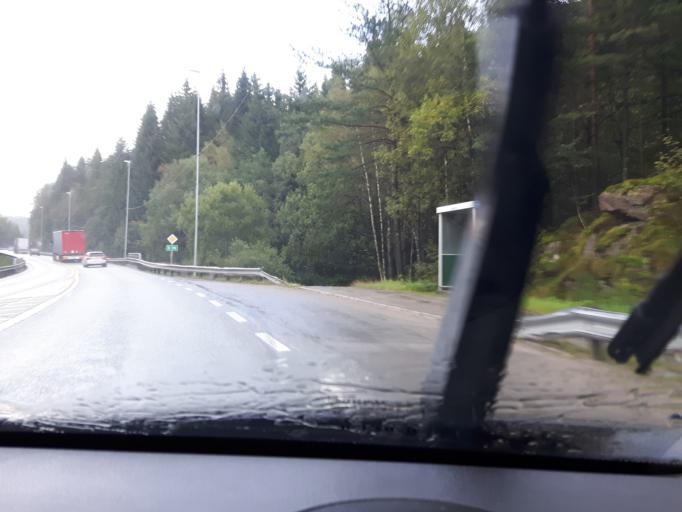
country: NO
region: Vest-Agder
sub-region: Sogne
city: Sogne
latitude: 58.0958
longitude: 7.7117
